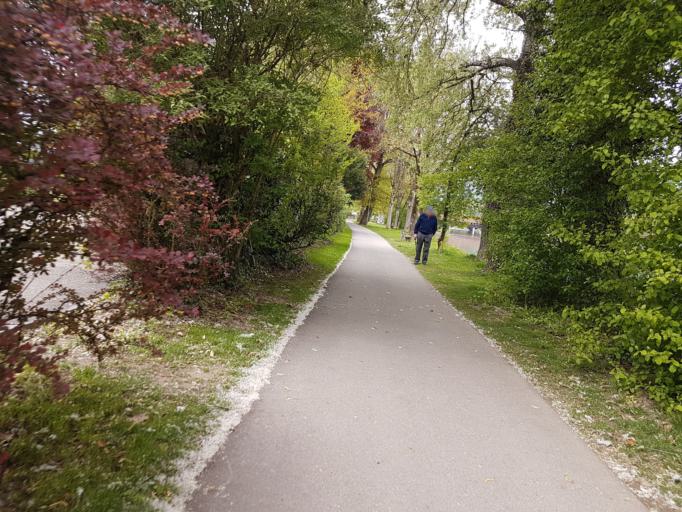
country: CH
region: Bern
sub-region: Oberaargau
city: Wangen an der Aare
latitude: 47.2354
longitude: 7.6593
